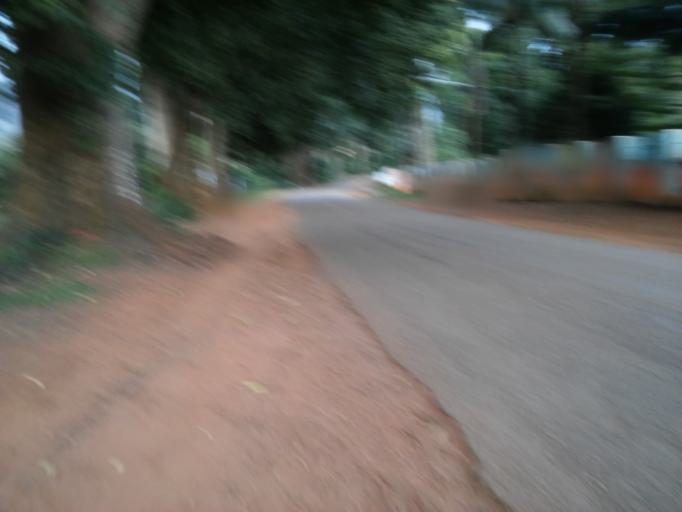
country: UG
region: Eastern Region
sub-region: Mbale District
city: Mbale
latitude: 1.0670
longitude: 34.1965
